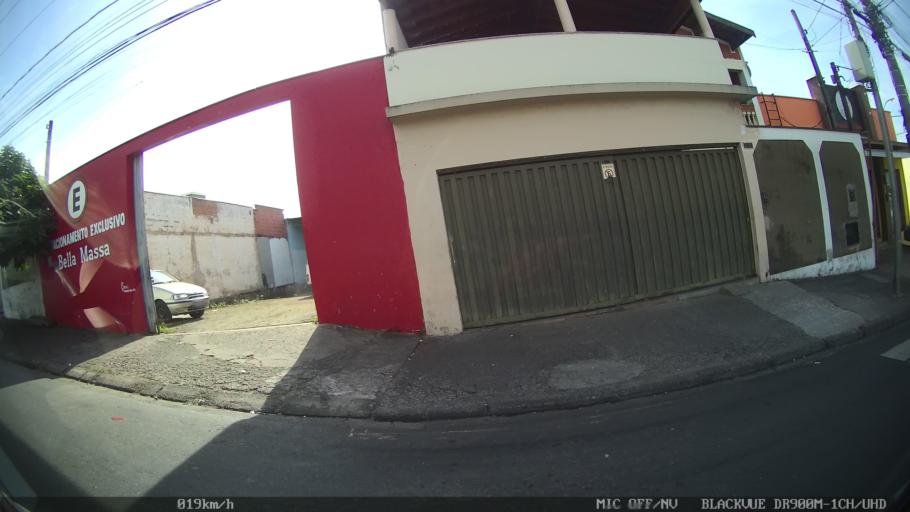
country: BR
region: Sao Paulo
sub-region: Piracicaba
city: Piracicaba
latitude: -22.7474
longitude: -47.6581
